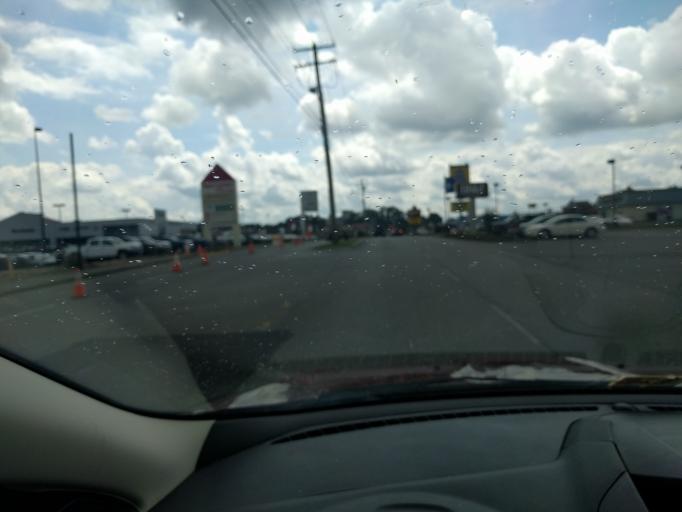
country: US
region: West Virginia
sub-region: Nicholas County
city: Summersville
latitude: 38.3056
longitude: -80.8322
